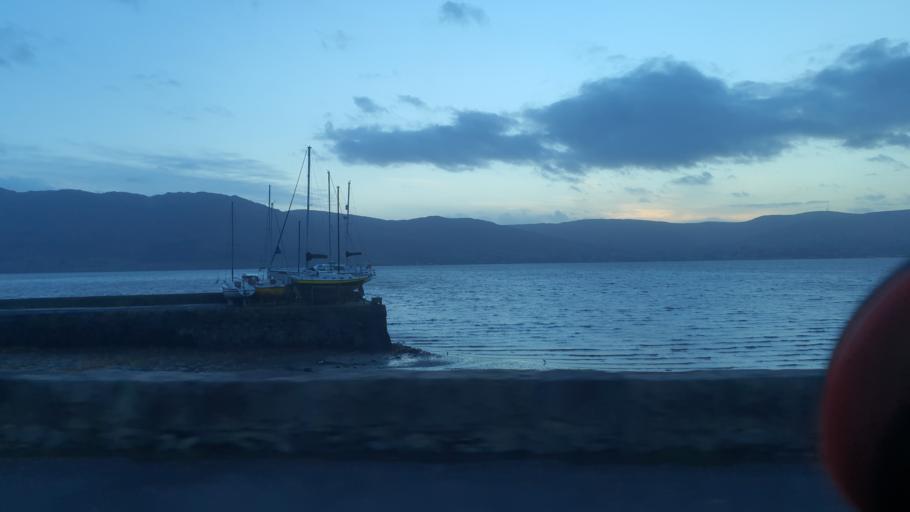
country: GB
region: Northern Ireland
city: Rostrevor
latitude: 54.0941
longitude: -6.1907
